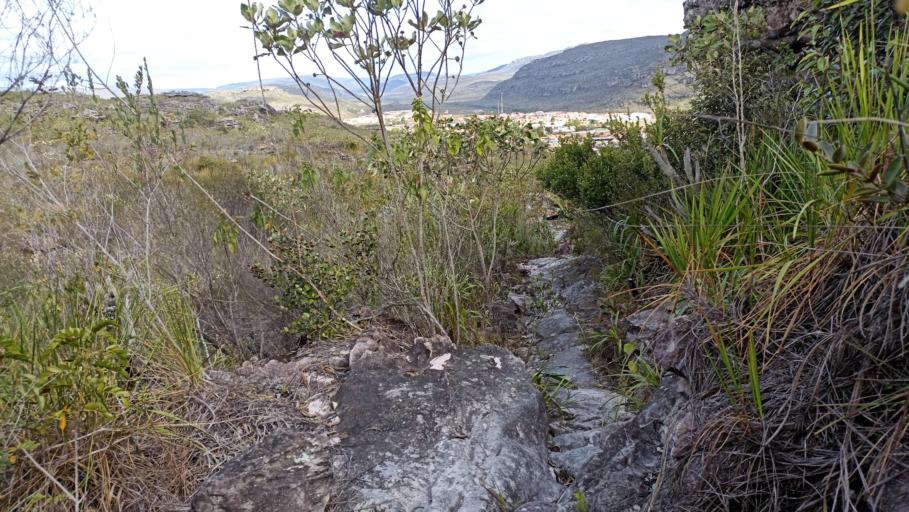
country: BR
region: Bahia
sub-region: Andarai
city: Vera Cruz
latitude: -12.9970
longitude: -41.3765
